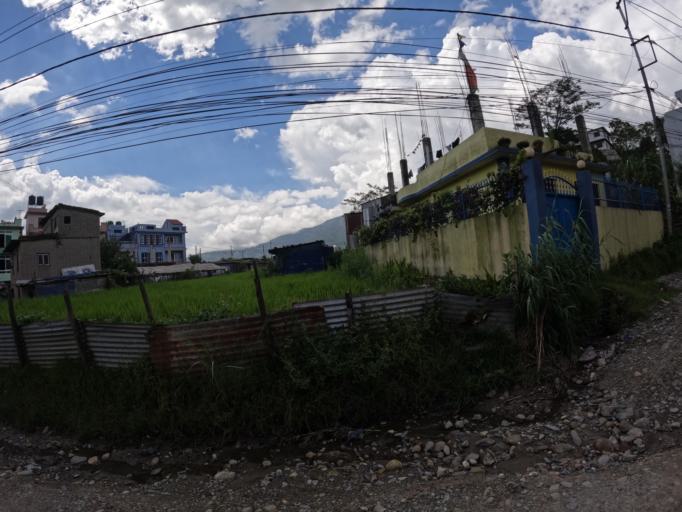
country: NP
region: Central Region
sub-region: Bagmati Zone
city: Kathmandu
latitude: 27.7654
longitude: 85.3266
